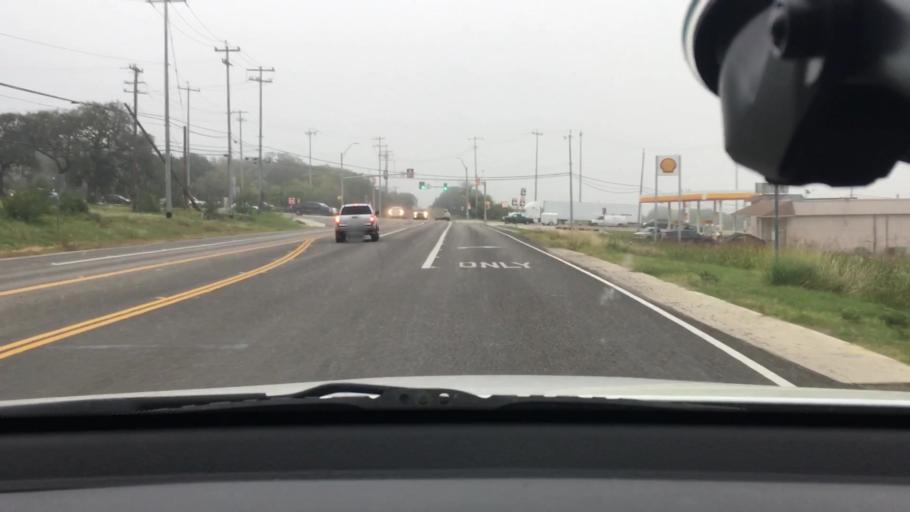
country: US
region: Texas
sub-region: Comal County
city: Garden Ridge
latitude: 29.6224
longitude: -98.2919
